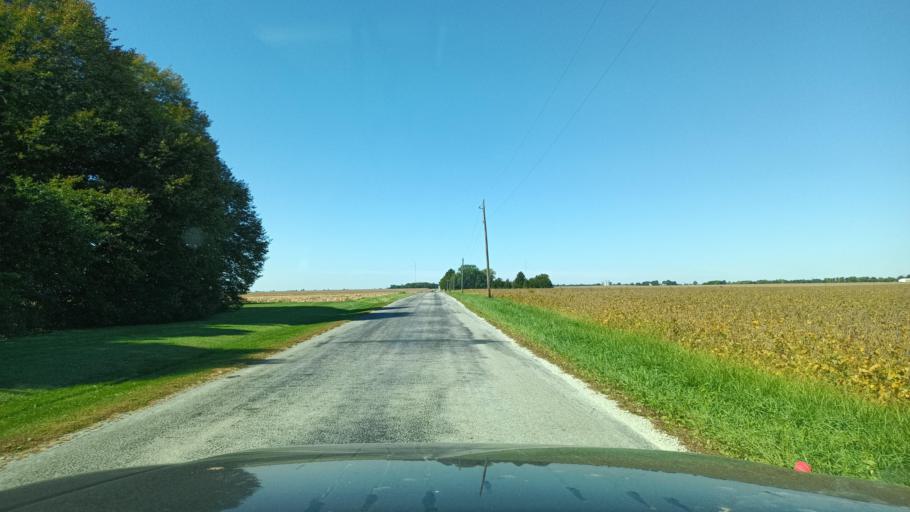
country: US
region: Illinois
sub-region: Champaign County
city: Mahomet
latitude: 40.0987
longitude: -88.3753
